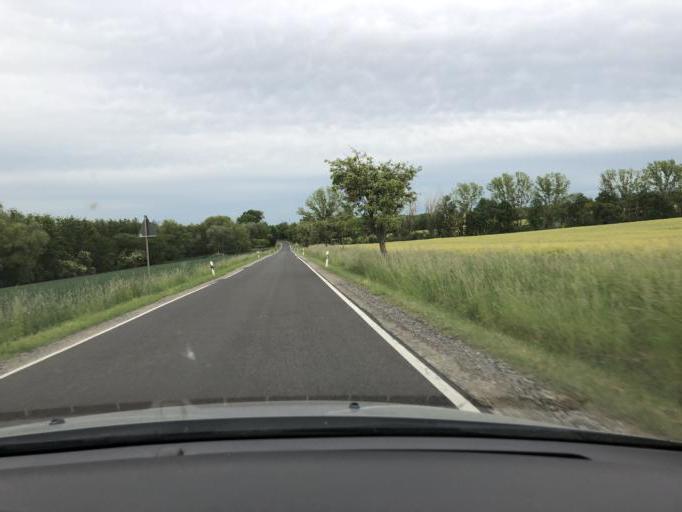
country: DE
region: Thuringia
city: Willerstedt
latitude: 51.0826
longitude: 11.4467
